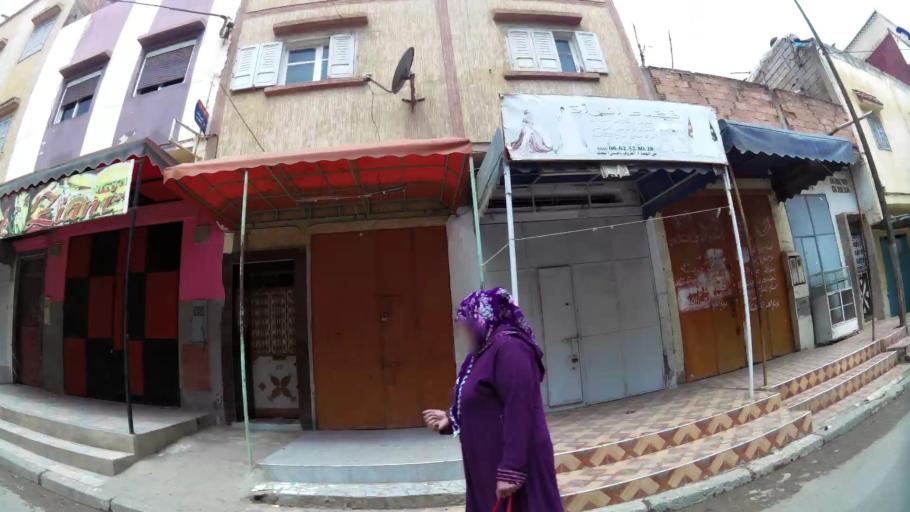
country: MA
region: Rabat-Sale-Zemmour-Zaer
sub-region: Khemisset
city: Tiflet
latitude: 33.8909
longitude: -6.3182
